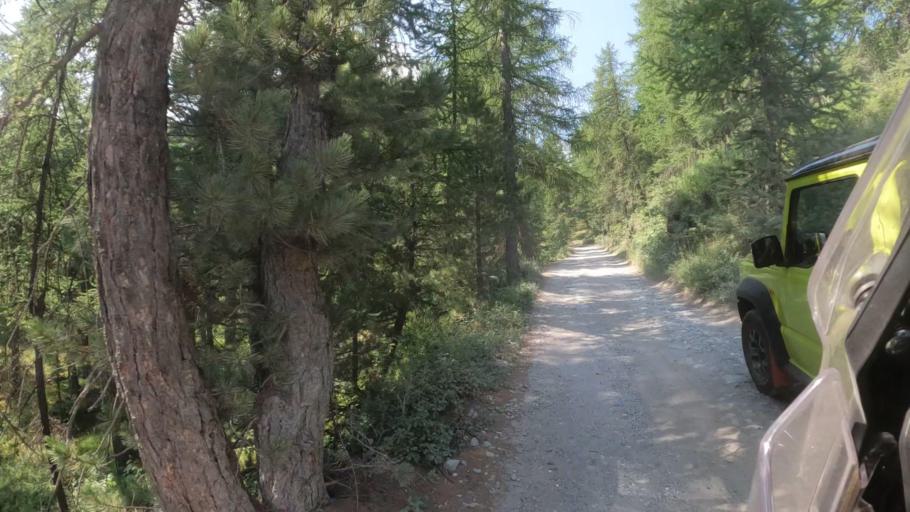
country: IT
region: Piedmont
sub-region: Provincia di Torino
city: Cesana Torinese
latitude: 44.9196
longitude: 6.8058
